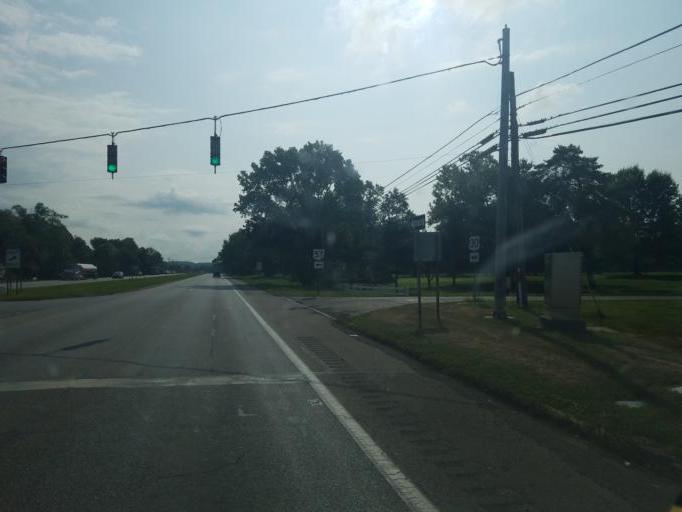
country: US
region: Ohio
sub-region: Wayne County
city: Orrville
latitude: 40.7965
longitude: -81.7658
